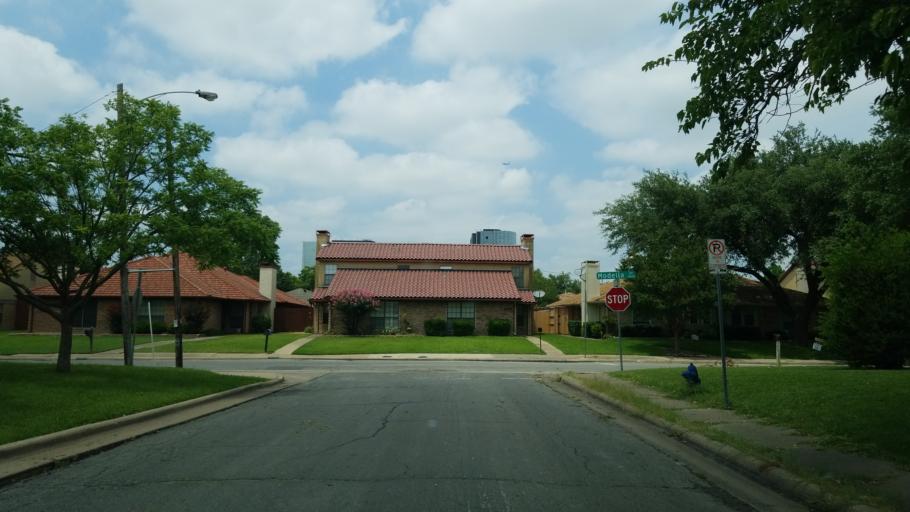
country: US
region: Texas
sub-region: Dallas County
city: Farmers Branch
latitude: 32.9065
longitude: -96.8769
